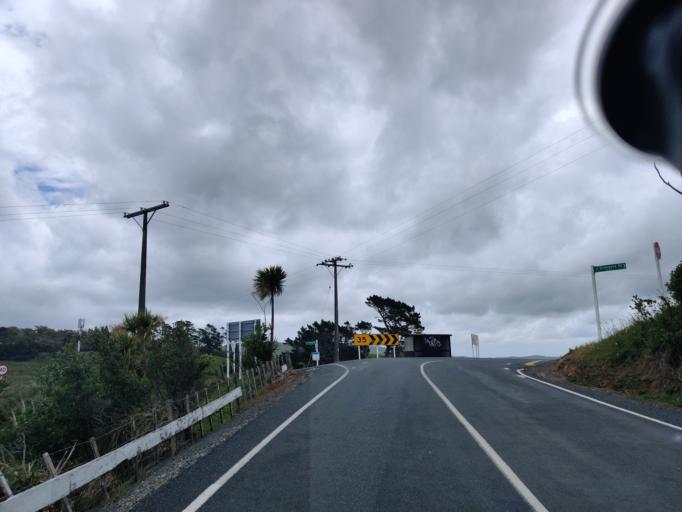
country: NZ
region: Auckland
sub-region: Auckland
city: Warkworth
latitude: -36.2782
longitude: 174.7744
